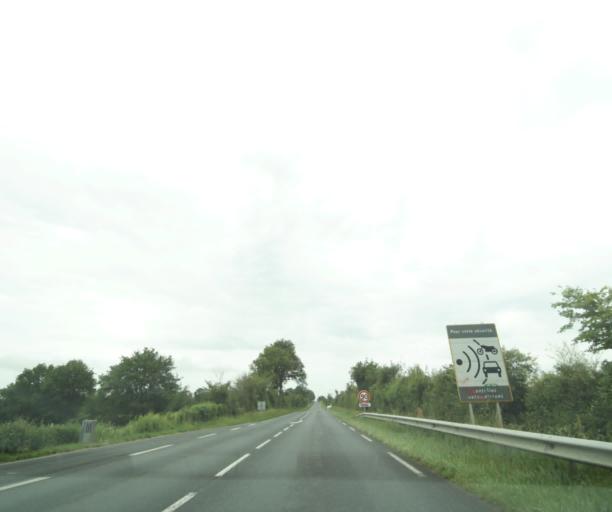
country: FR
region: Poitou-Charentes
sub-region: Departement des Deux-Sevres
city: Viennay
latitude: 46.7189
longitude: -0.2387
